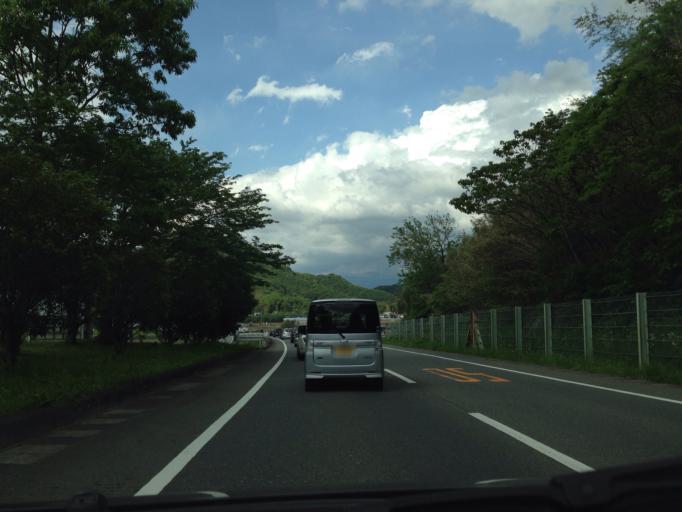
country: JP
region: Shizuoka
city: Mishima
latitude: 35.0514
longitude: 138.9236
